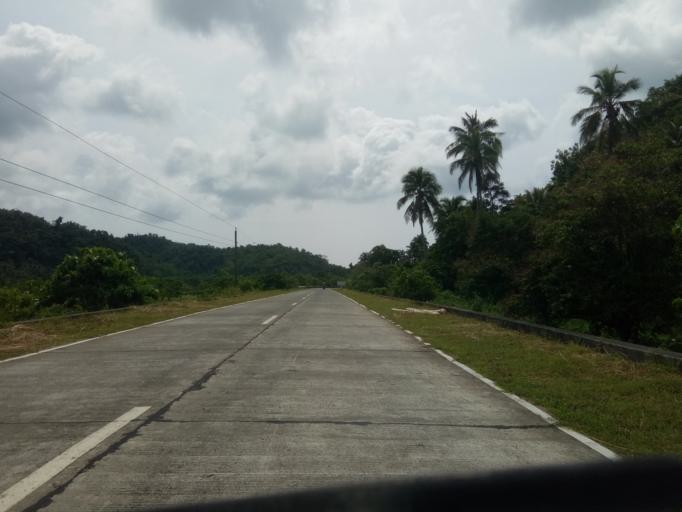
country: PH
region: Caraga
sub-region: Province of Surigao del Norte
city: Pilar
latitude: 9.8922
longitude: 126.0769
